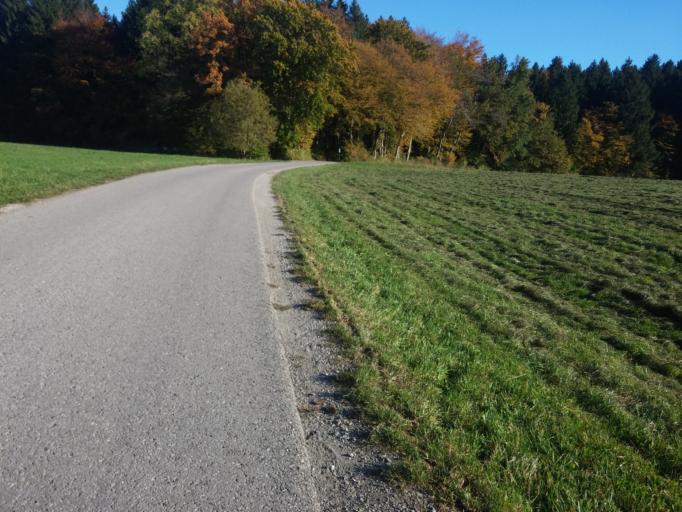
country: DE
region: Bavaria
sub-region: Upper Bavaria
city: Aying
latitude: 47.9658
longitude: 11.7880
